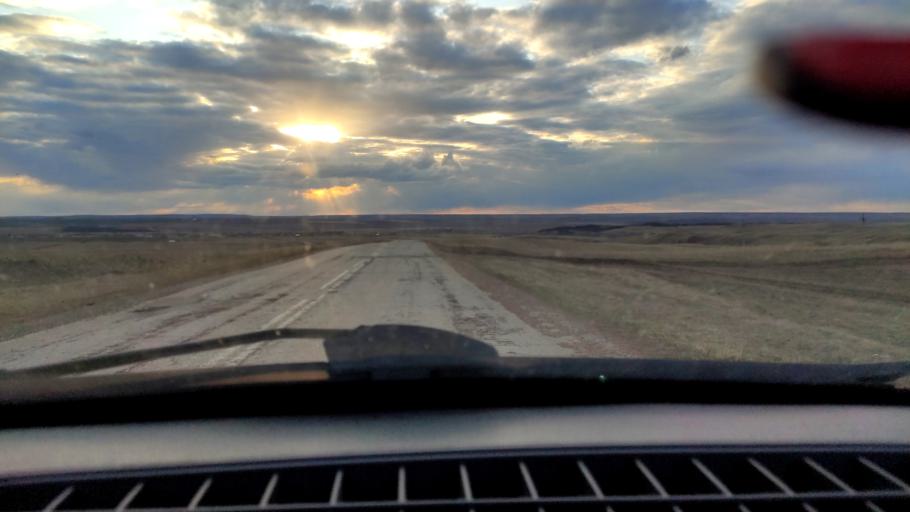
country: RU
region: Bashkortostan
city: Tolbazy
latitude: 54.0117
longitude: 55.5706
